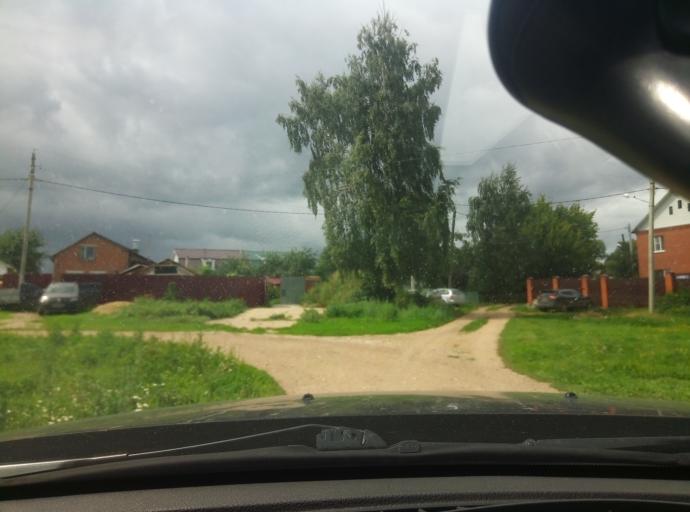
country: RU
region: Tula
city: Novomoskovsk
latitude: 53.9980
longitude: 38.2942
